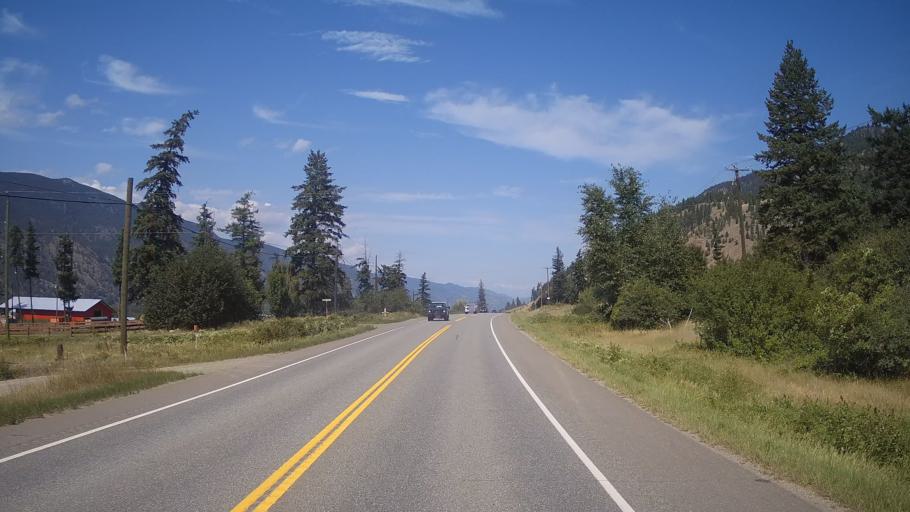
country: CA
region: British Columbia
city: Kamloops
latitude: 50.9239
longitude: -120.2359
